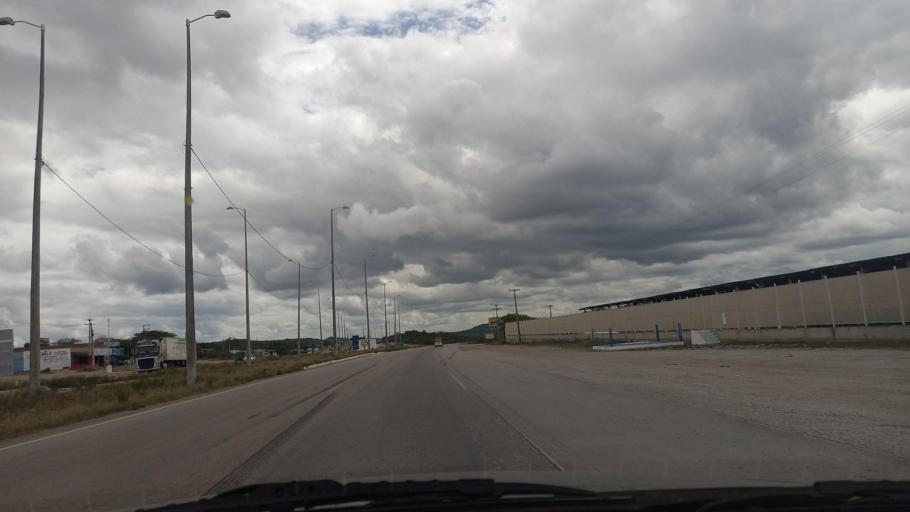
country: BR
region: Pernambuco
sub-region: Caruaru
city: Caruaru
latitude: -8.3207
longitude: -36.0791
